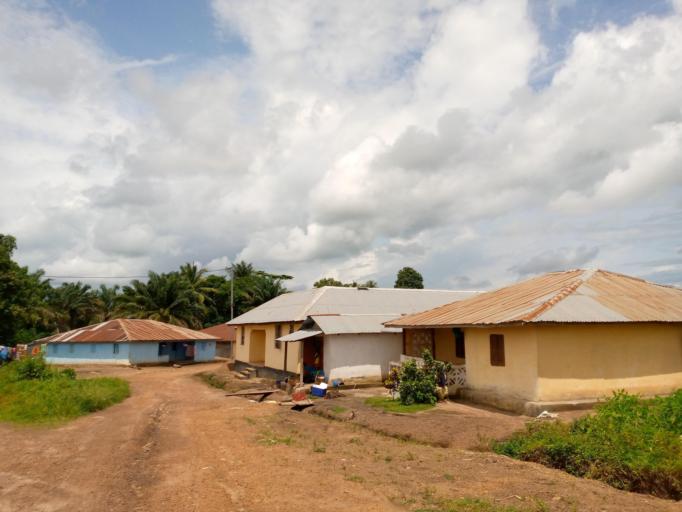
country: SL
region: Northern Province
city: Magburaka
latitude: 8.7177
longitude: -11.9612
